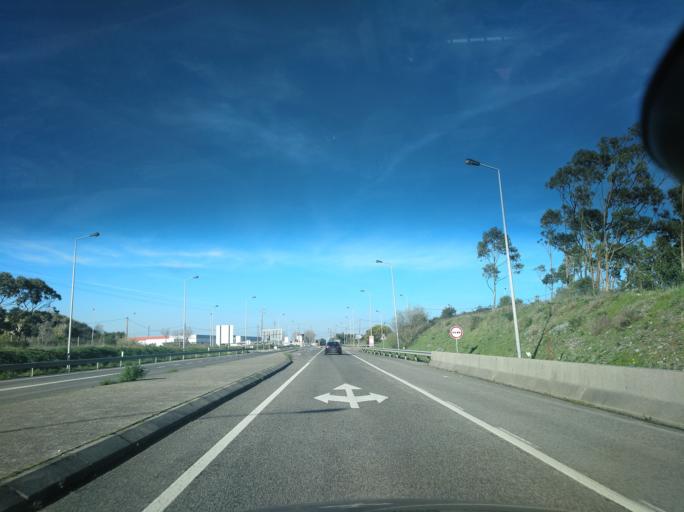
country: PT
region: Lisbon
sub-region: Sintra
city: Pero Pinheiro
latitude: 38.8718
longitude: -9.3296
